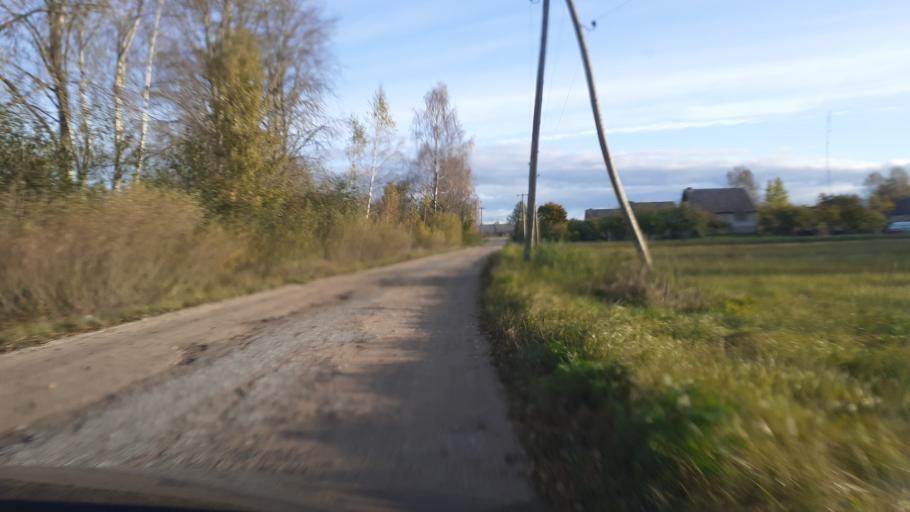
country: LV
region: Kuldigas Rajons
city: Kuldiga
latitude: 56.8796
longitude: 22.1102
